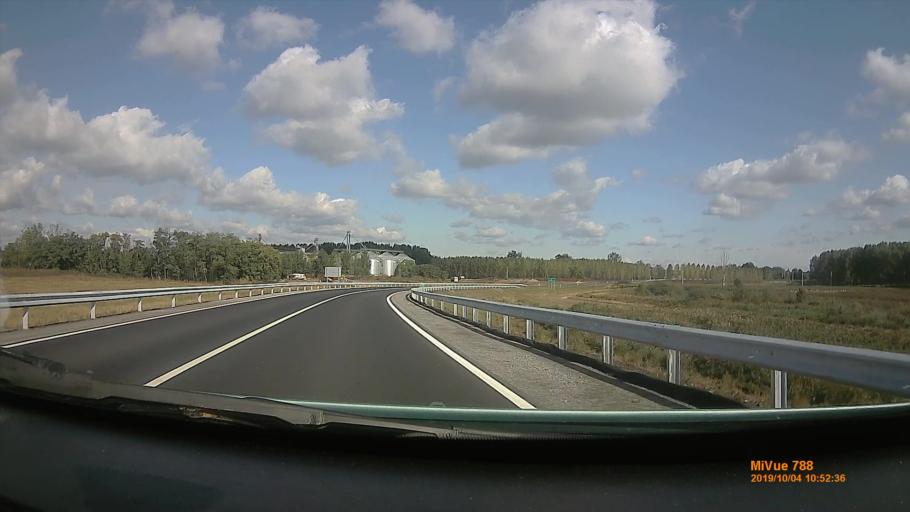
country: HU
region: Szabolcs-Szatmar-Bereg
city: Nyirtelek
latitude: 47.9830
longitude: 21.6660
